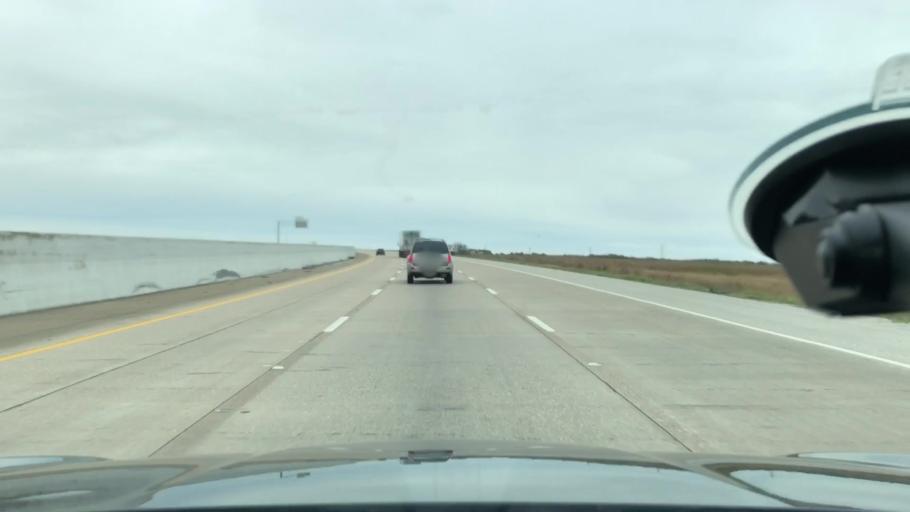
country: US
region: Texas
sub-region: Ellis County
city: Italy
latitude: 32.1432
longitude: -96.9398
